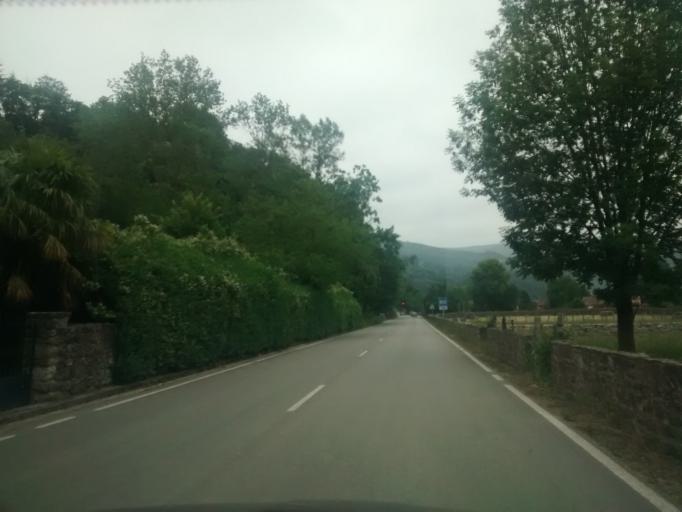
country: ES
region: Cantabria
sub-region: Provincia de Cantabria
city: Ruente
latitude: 43.2117
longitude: -4.3015
